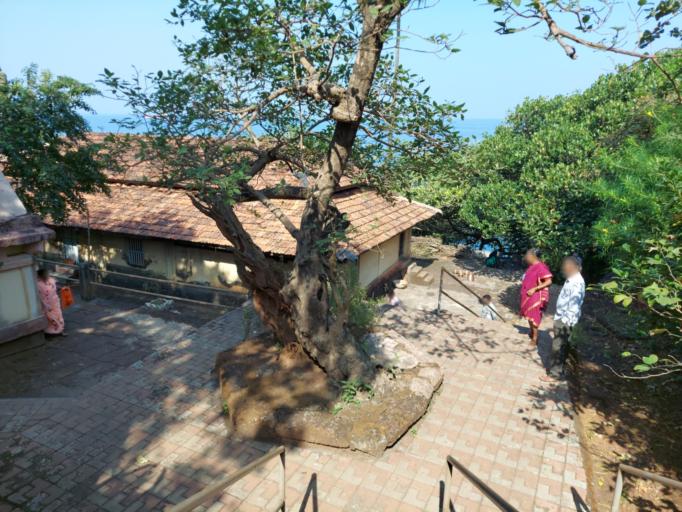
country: IN
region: Maharashtra
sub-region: Ratnagiri
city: Guhagar
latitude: 17.3045
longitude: 73.1942
